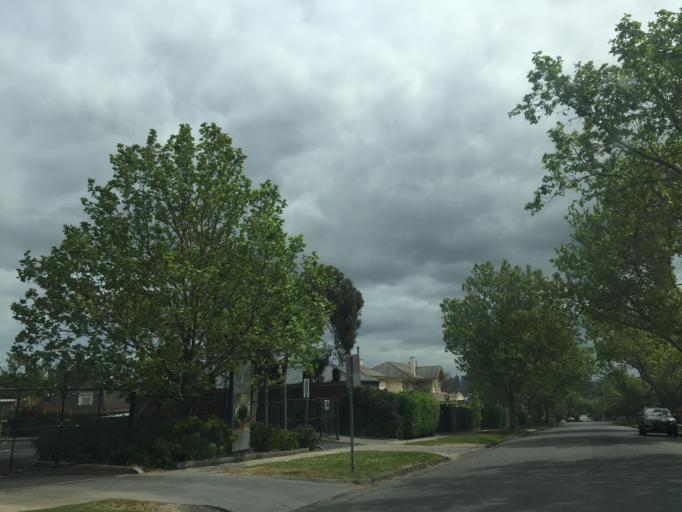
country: AU
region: Victoria
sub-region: Boroondara
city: Hawthorn East
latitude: -37.8127
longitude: 145.0489
